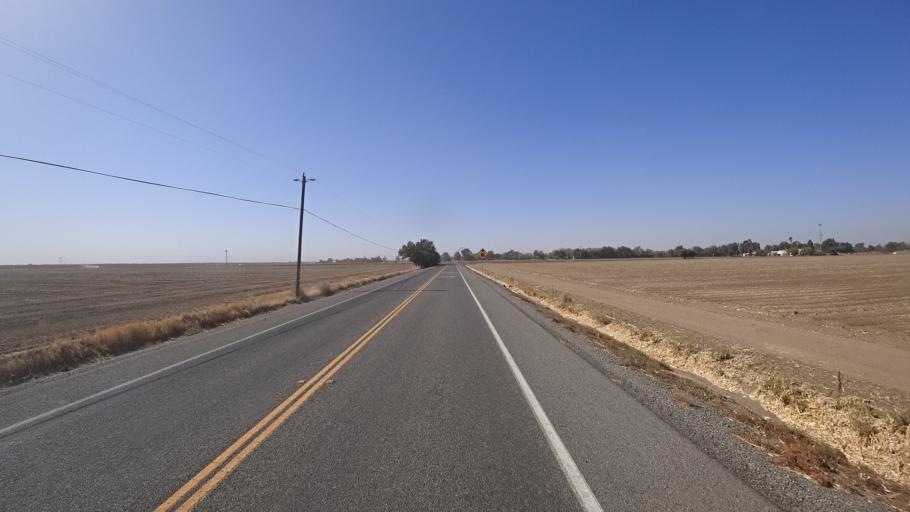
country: US
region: California
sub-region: Yolo County
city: Davis
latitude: 38.5904
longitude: -121.7833
